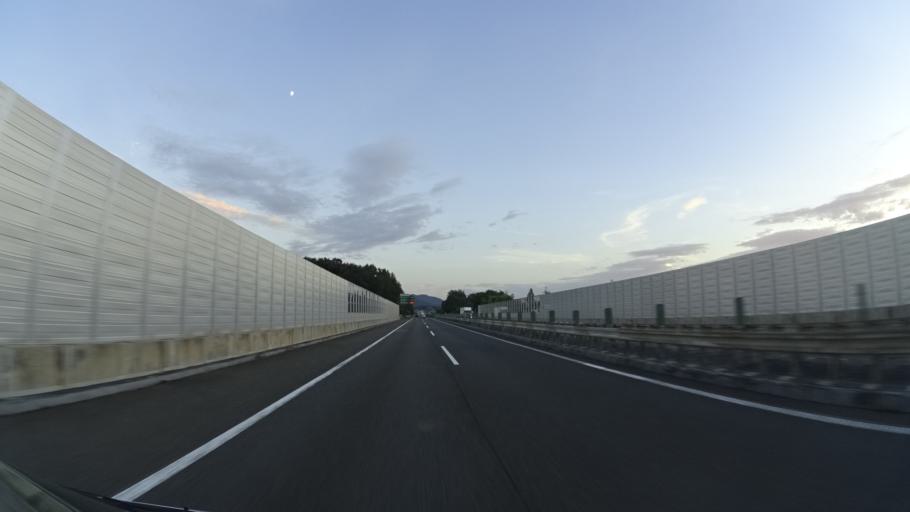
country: JP
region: Shiga Prefecture
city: Hikone
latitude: 35.2476
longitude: 136.2815
